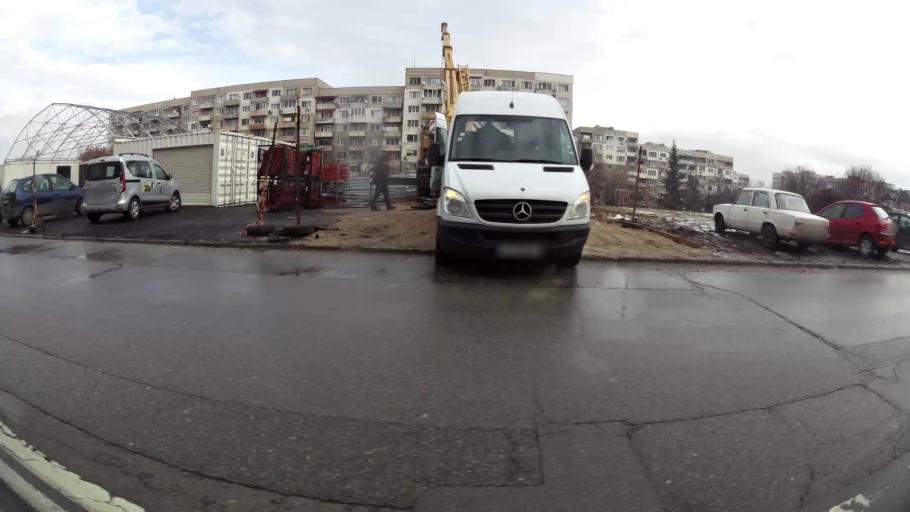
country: BG
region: Sofiya
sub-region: Obshtina Bozhurishte
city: Bozhurishte
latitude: 42.7245
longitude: 23.2458
